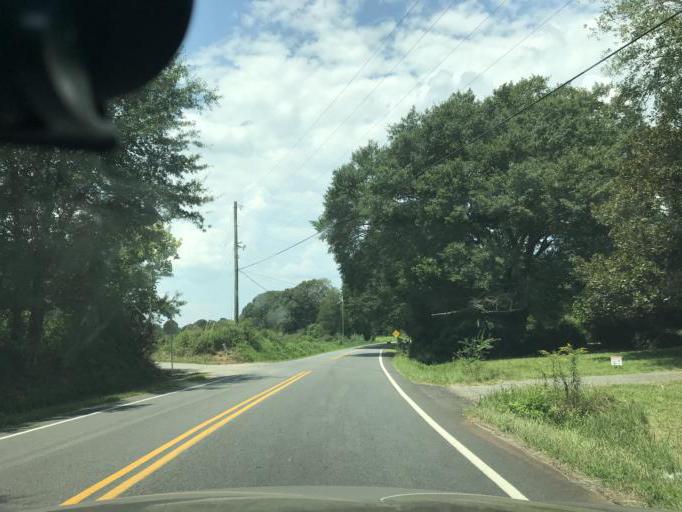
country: US
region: Georgia
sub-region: Dawson County
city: Dawsonville
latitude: 34.3349
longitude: -84.1318
